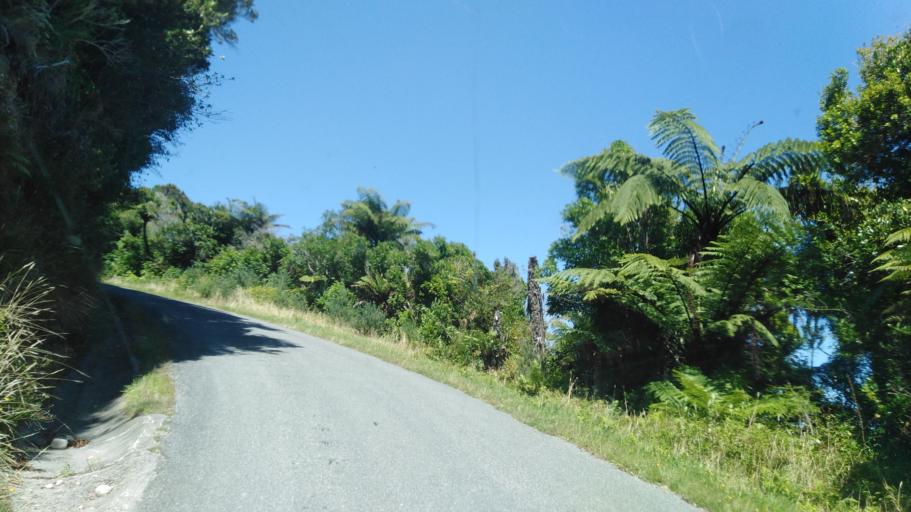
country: NZ
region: West Coast
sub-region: Buller District
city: Westport
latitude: -41.2605
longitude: 172.1130
